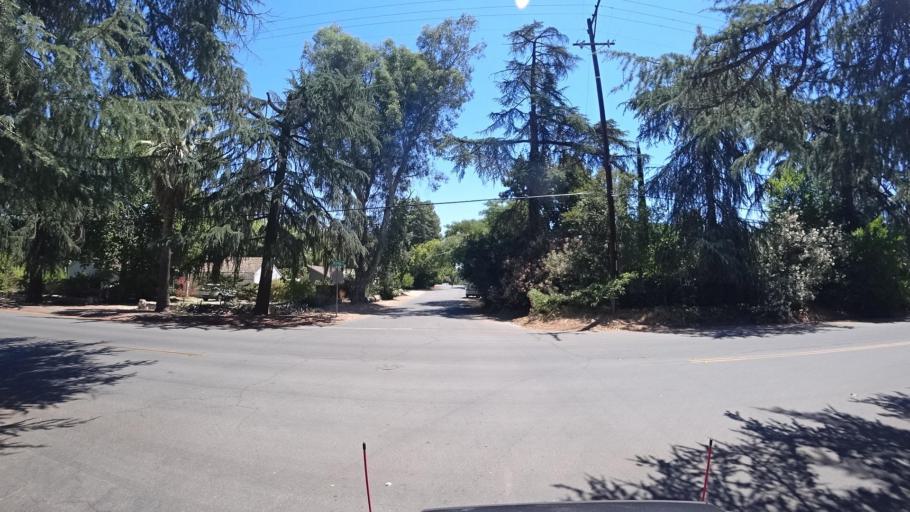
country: US
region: California
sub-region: Fresno County
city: Fresno
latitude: 36.7822
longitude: -119.8025
